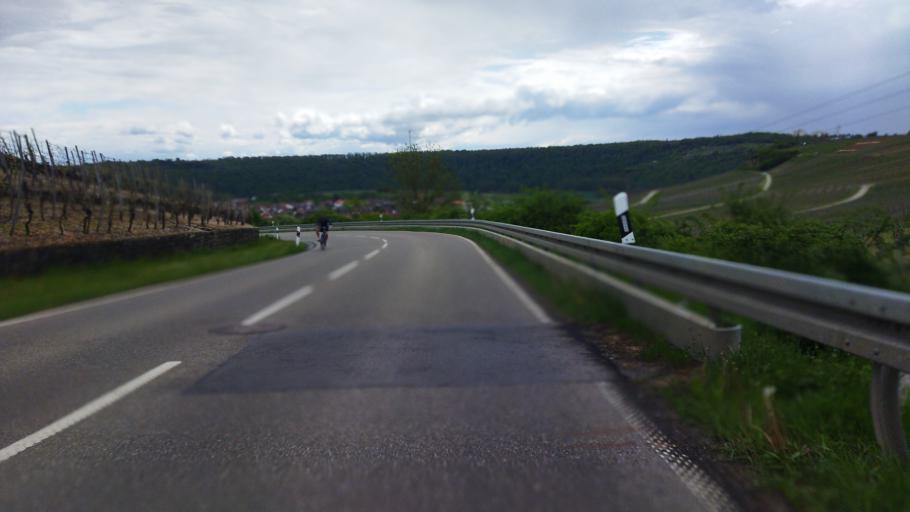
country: DE
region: Baden-Wuerttemberg
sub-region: Regierungsbezirk Stuttgart
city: Hessigheim
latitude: 49.0035
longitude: 9.1869
